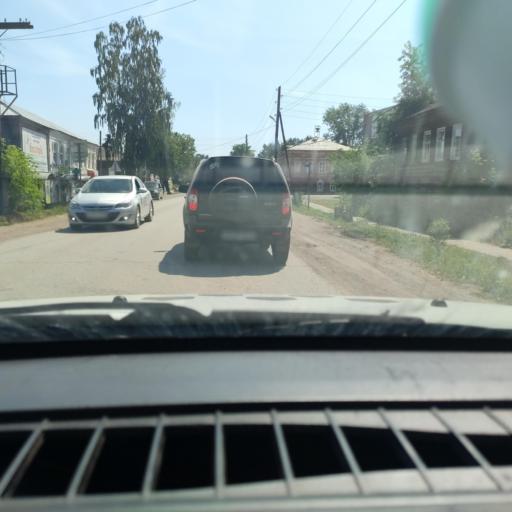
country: RU
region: Perm
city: Okhansk
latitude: 57.7233
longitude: 55.3896
